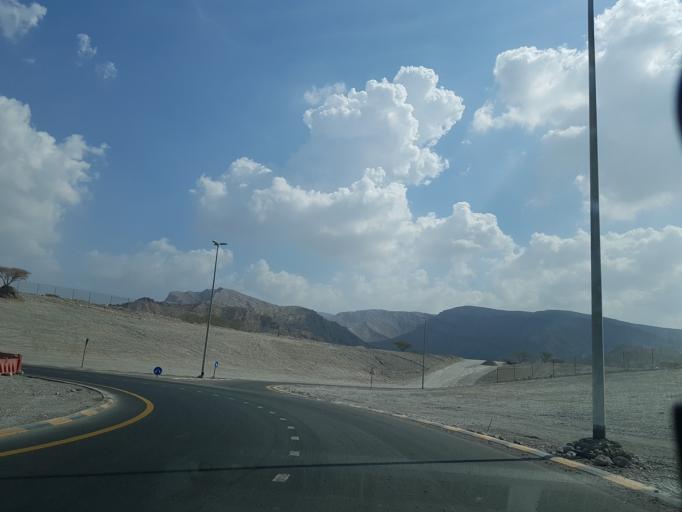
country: AE
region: Ra's al Khaymah
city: Ras al-Khaimah
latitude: 25.7624
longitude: 56.0231
